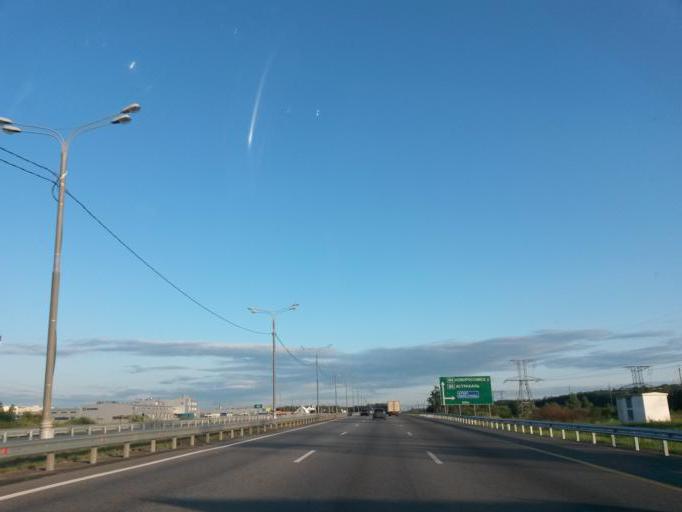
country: RU
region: Moskovskaya
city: Vostryakovo
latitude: 55.3769
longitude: 37.7792
